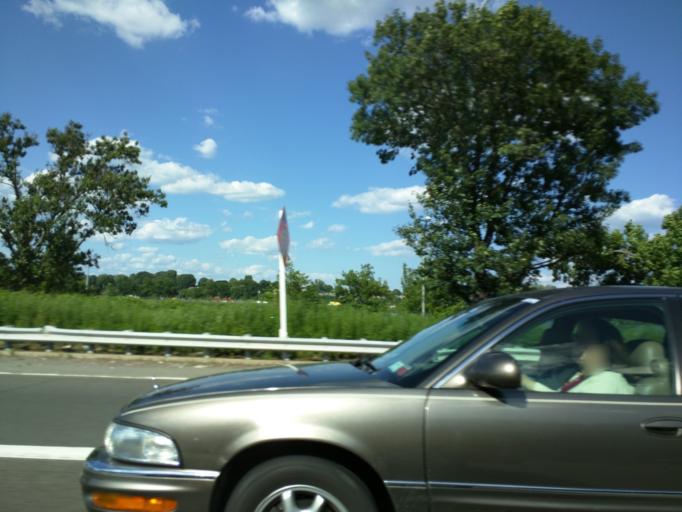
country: US
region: New York
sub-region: Queens County
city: Borough of Queens
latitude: 40.7292
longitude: -73.8396
